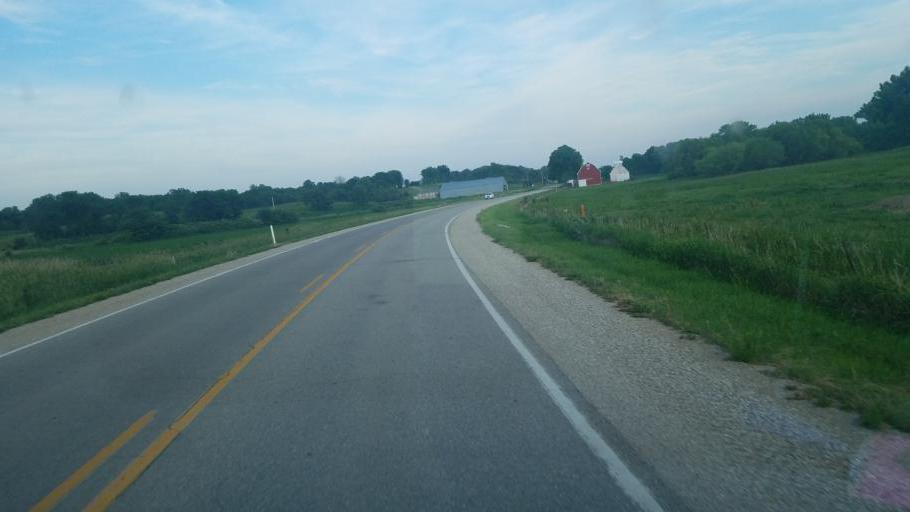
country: US
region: Iowa
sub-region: Benton County
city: Belle Plaine
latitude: 41.9347
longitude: -92.4019
